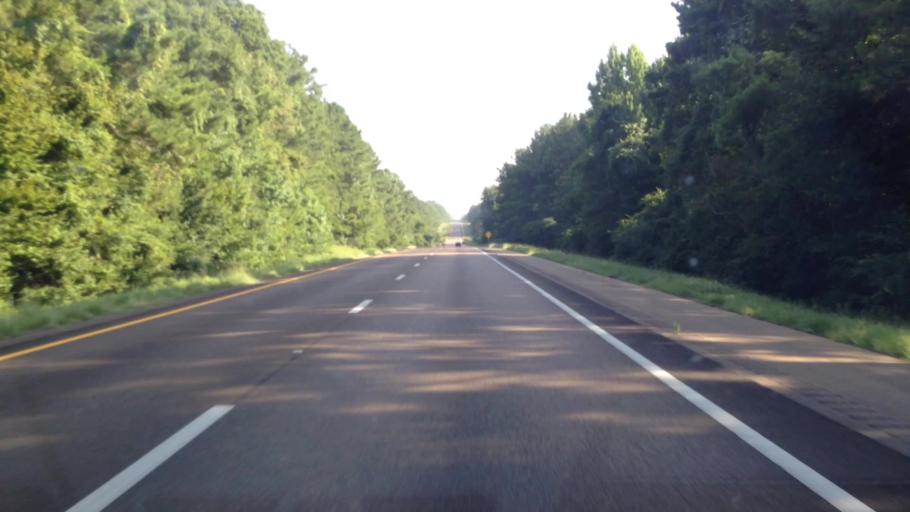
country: US
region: Mississippi
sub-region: Pike County
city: Summit
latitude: 31.3765
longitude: -90.4791
